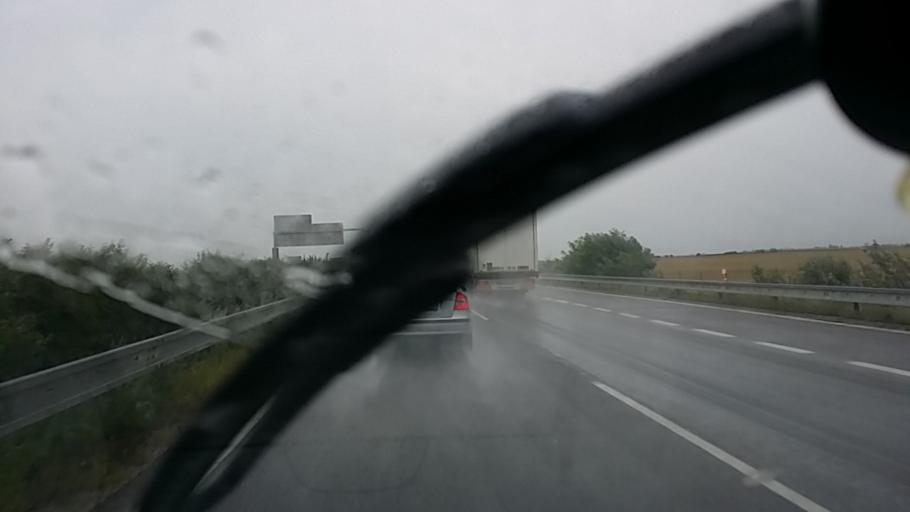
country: AT
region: Burgenland
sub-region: Politischer Bezirk Neusiedl am See
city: Kittsee
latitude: 48.0670
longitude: 17.1016
